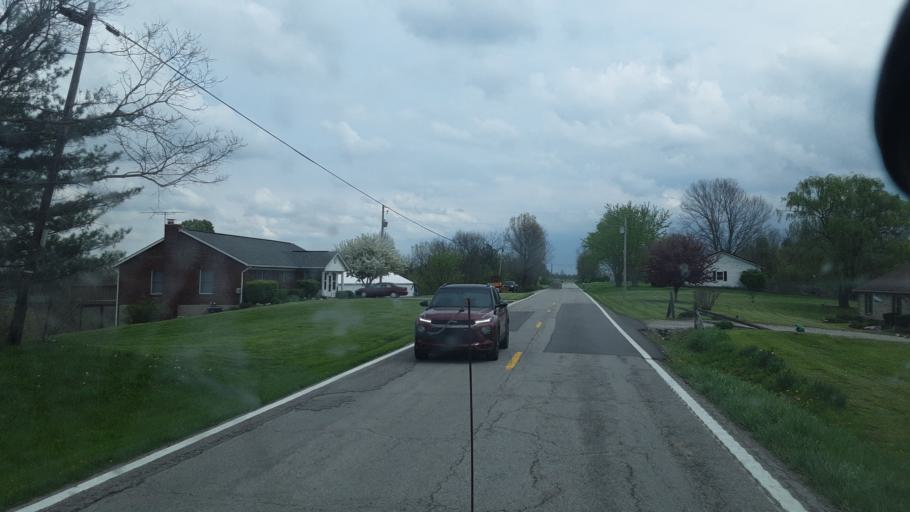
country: US
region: Kentucky
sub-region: Grant County
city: Dry Ridge
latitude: 38.6623
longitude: -84.6609
